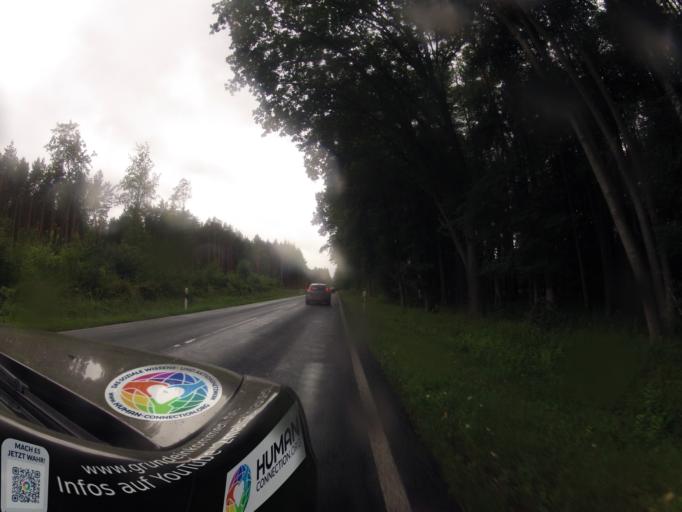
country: DE
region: Mecklenburg-Vorpommern
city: Usedom
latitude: 53.8908
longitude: 13.9595
